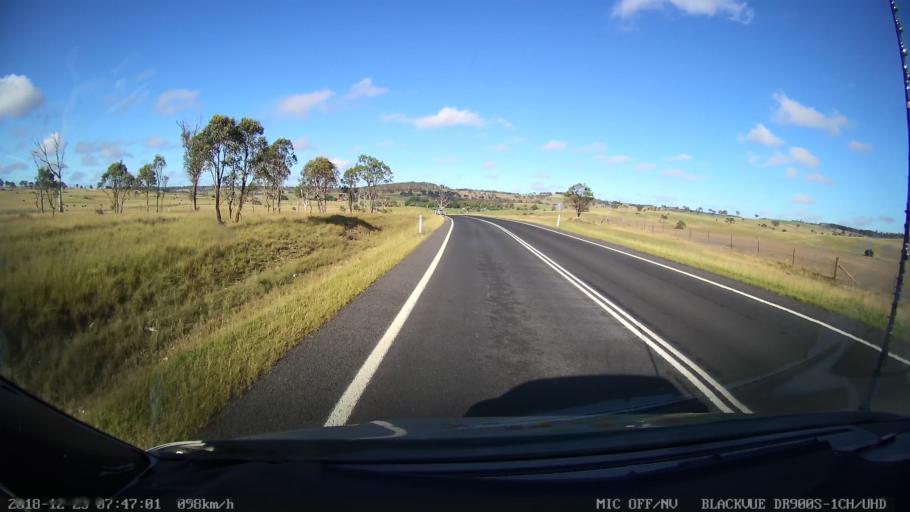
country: AU
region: New South Wales
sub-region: Armidale Dumaresq
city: Enmore
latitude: -30.5256
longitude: 151.9085
